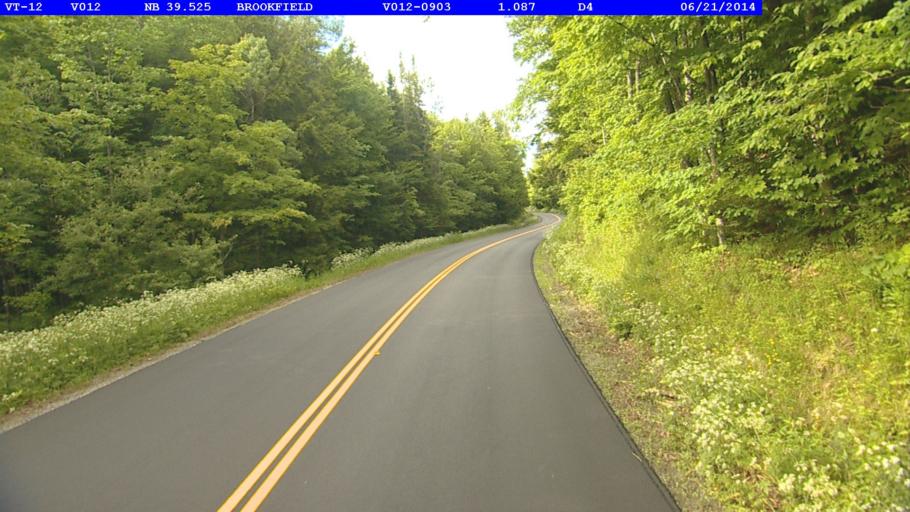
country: US
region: Vermont
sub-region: Orange County
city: Randolph
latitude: 44.0201
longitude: -72.6576
